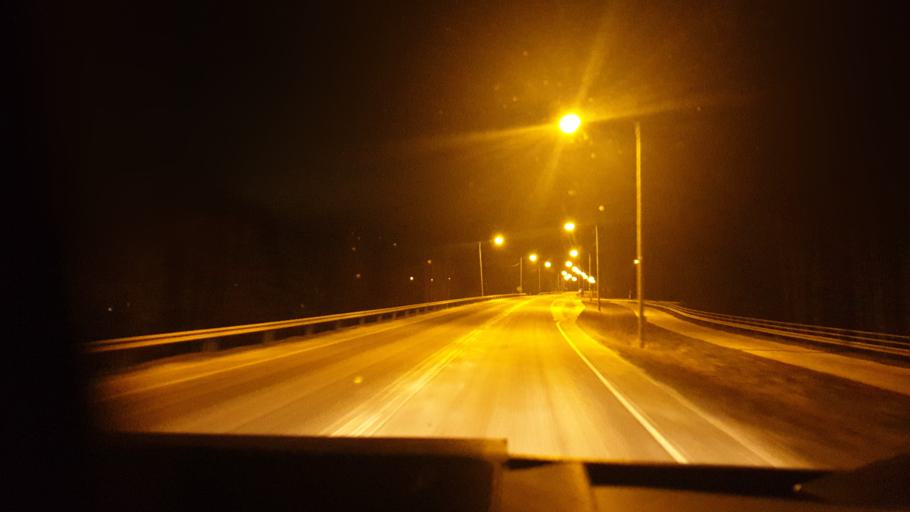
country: FI
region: Southern Ostrobothnia
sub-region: Kuusiokunnat
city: Alavus
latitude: 62.5967
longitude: 23.6593
